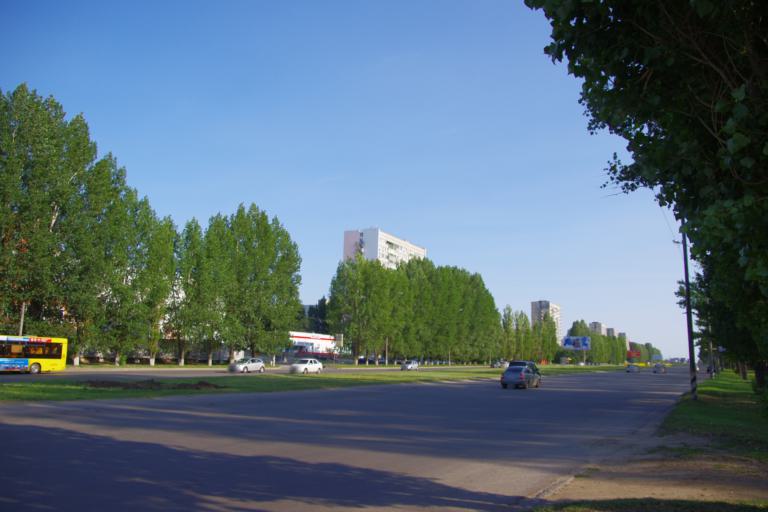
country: RU
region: Samara
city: Tol'yatti
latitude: 53.5146
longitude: 49.2777
